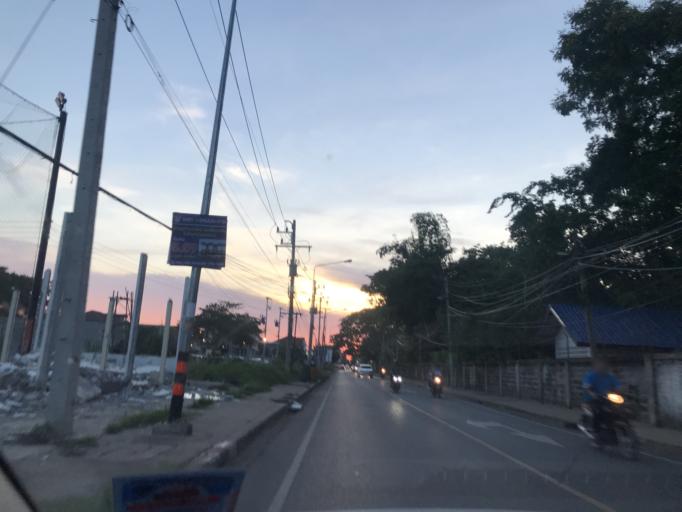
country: TH
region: Changwat Udon Thani
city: Udon Thani
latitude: 17.4007
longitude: 102.7774
